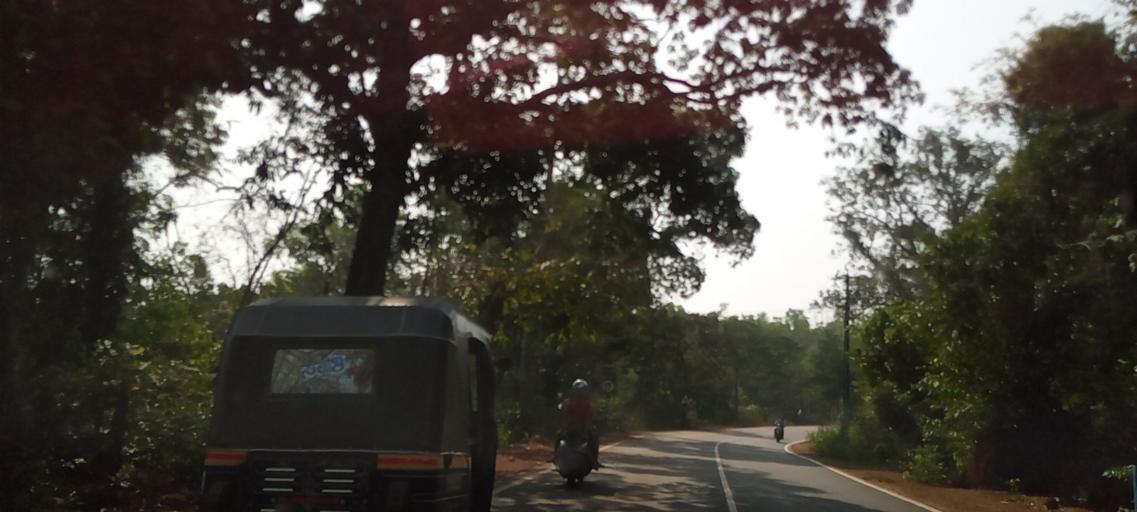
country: IN
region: Karnataka
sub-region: Udupi
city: Someshwar
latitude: 13.5405
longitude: 74.9144
